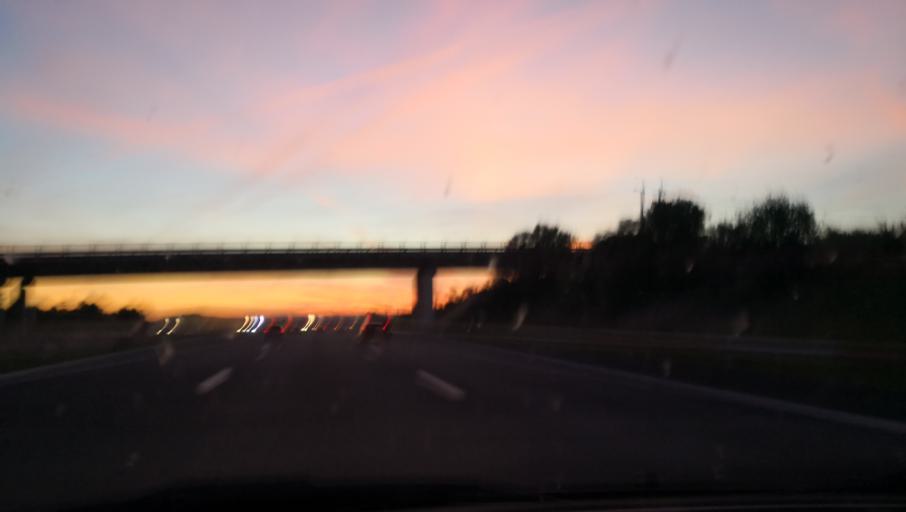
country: PT
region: Santarem
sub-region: Cartaxo
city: Pontevel
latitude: 39.1787
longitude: -8.8342
